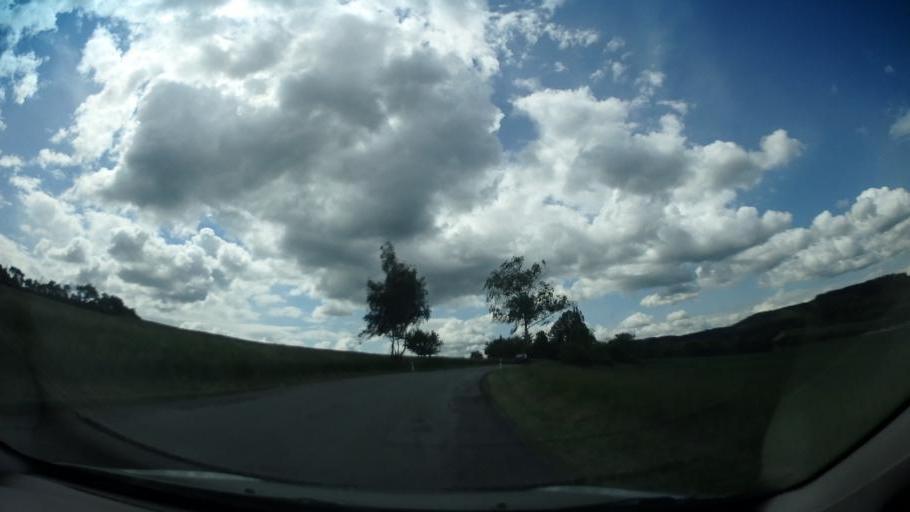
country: CZ
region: South Moravian
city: Velke Opatovice
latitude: 49.6233
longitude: 16.6085
